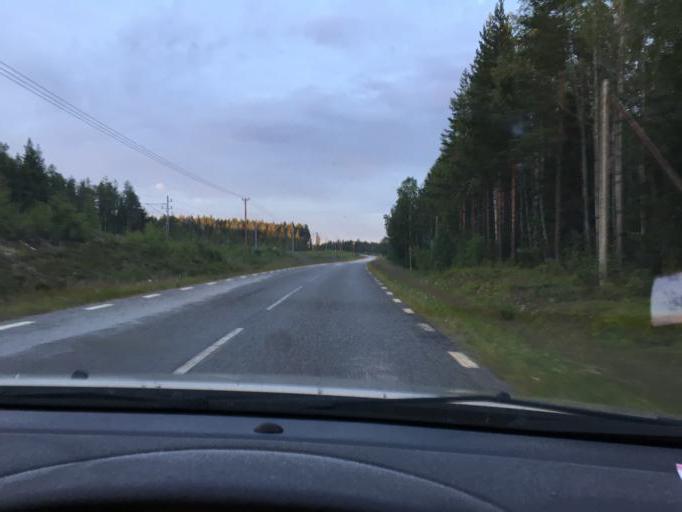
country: SE
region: Norrbotten
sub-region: Kalix Kommun
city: Toere
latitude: 66.0537
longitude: 22.5677
